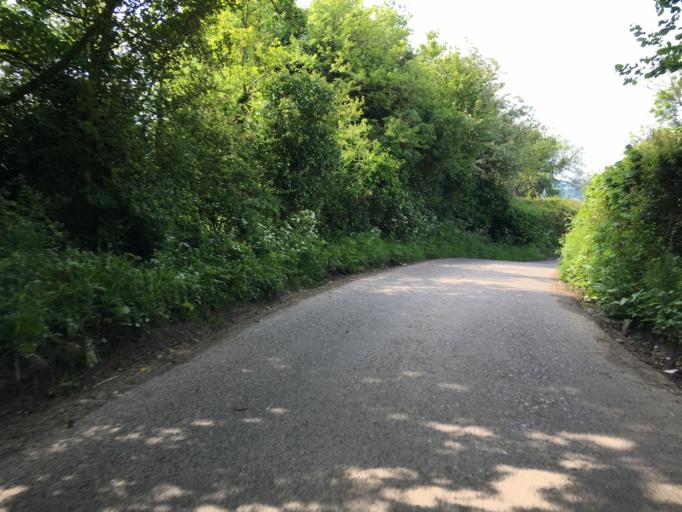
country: GB
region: England
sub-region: North Somerset
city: Winford
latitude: 51.3874
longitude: -2.6525
